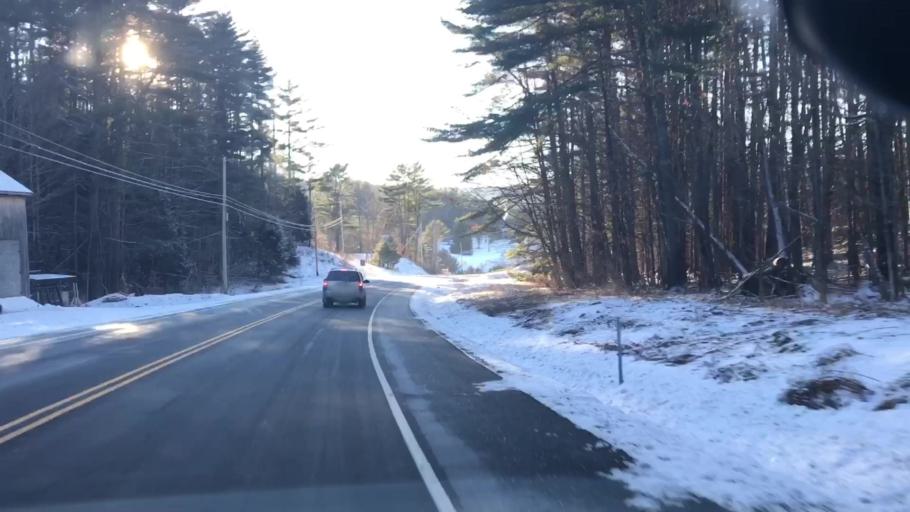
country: US
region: New Hampshire
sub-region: Grafton County
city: Haverhill
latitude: 43.9615
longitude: -72.0846
